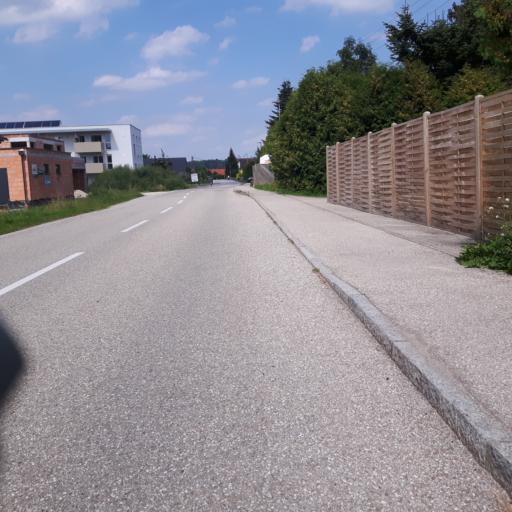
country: AT
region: Upper Austria
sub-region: Wels-Land
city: Stadl-Paura
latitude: 48.0785
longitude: 13.8704
